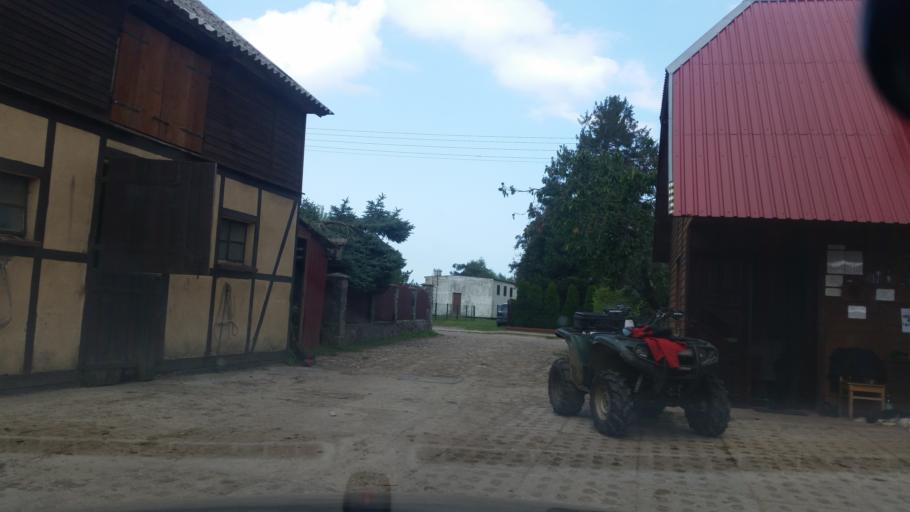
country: PL
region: Pomeranian Voivodeship
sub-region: Powiat wejherowski
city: Choczewo
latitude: 54.7695
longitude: 17.7974
